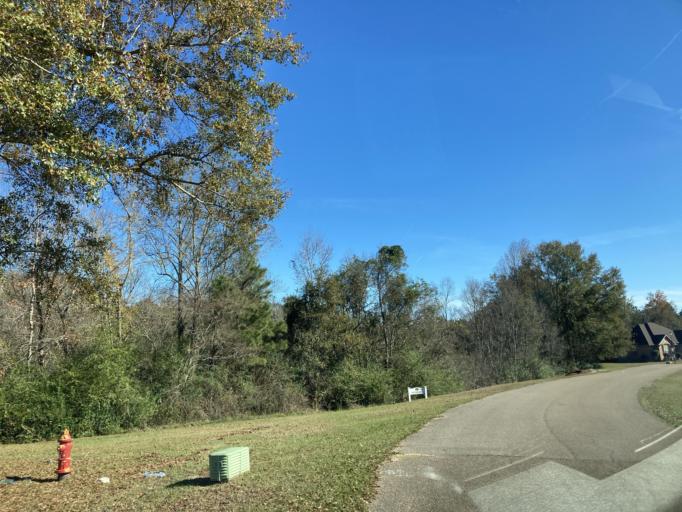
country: US
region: Mississippi
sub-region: Forrest County
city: Petal
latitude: 31.3172
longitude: -89.1852
